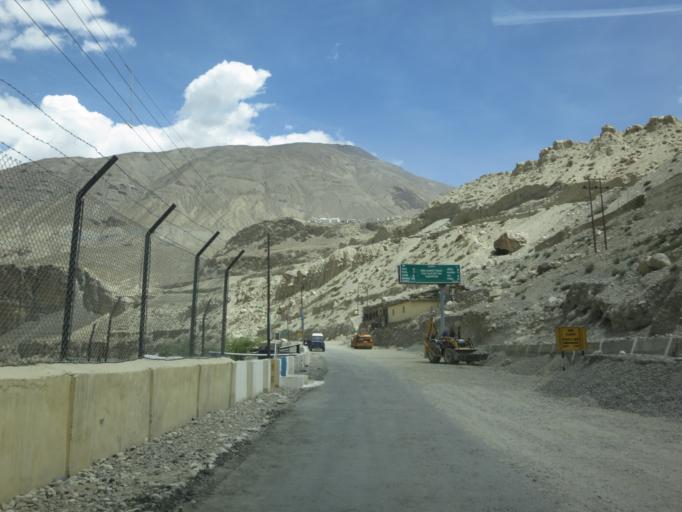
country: CN
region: Tibet Autonomous Region
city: Diyag
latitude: 32.0520
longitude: 78.6067
